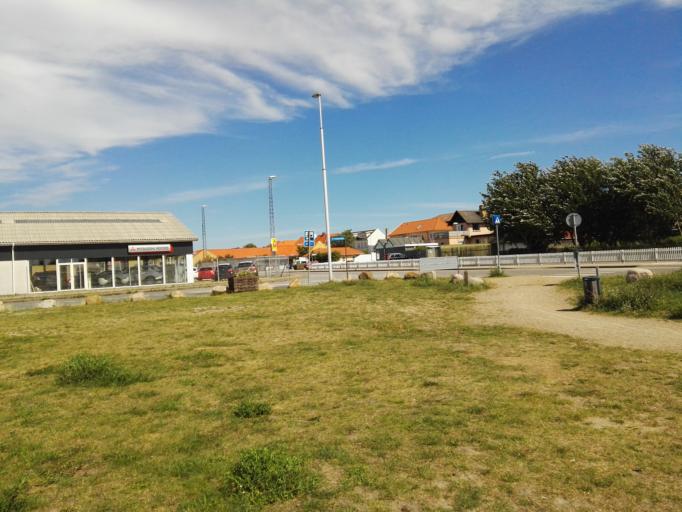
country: DK
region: Capital Region
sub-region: Halsnaes Kommune
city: Hundested
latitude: 55.9623
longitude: 11.8498
